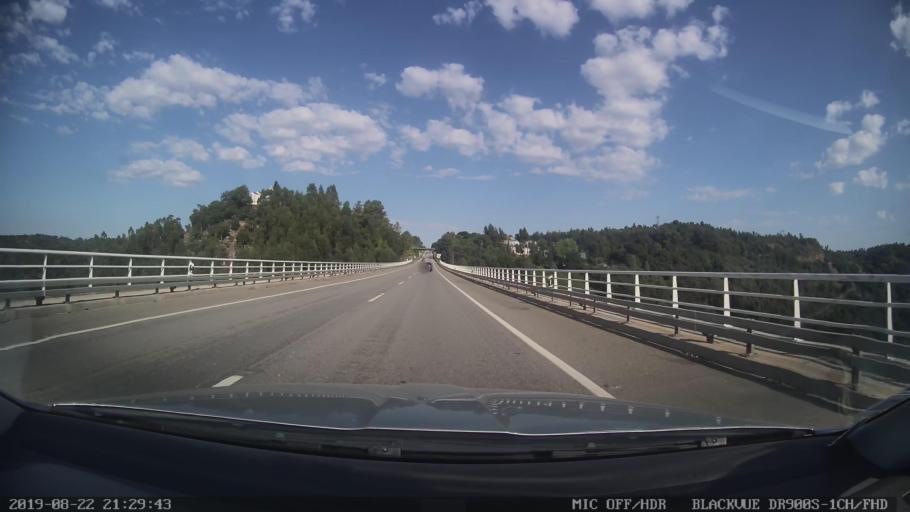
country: PT
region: Leiria
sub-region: Pedrogao Grande
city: Pedrogao Grande
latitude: 39.9044
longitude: -8.1399
